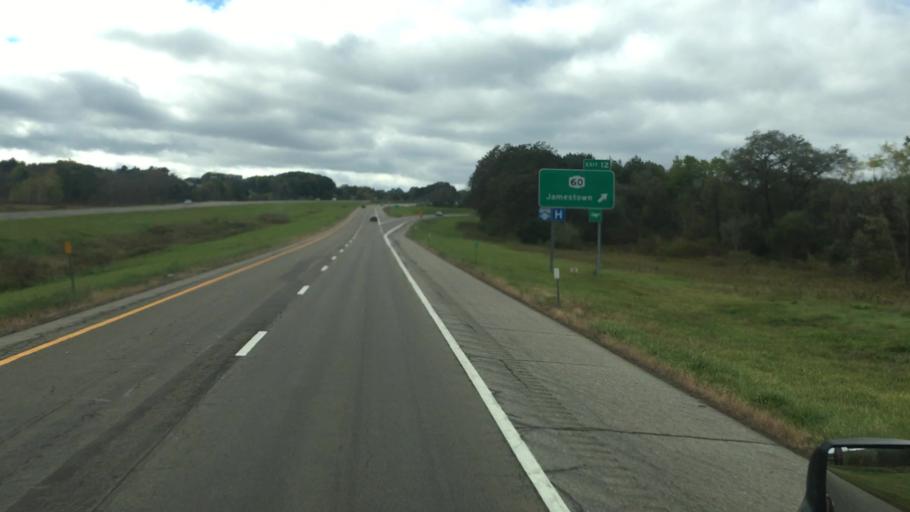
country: US
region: New York
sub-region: Chautauqua County
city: Jamestown
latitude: 42.1240
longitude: -79.2320
